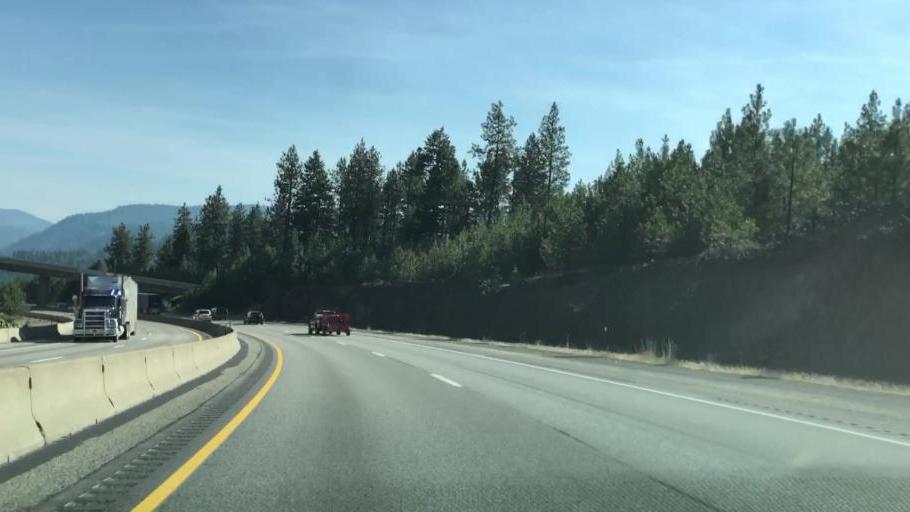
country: US
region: Idaho
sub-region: Kootenai County
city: Coeur d'Alene
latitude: 47.6338
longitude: -116.7075
